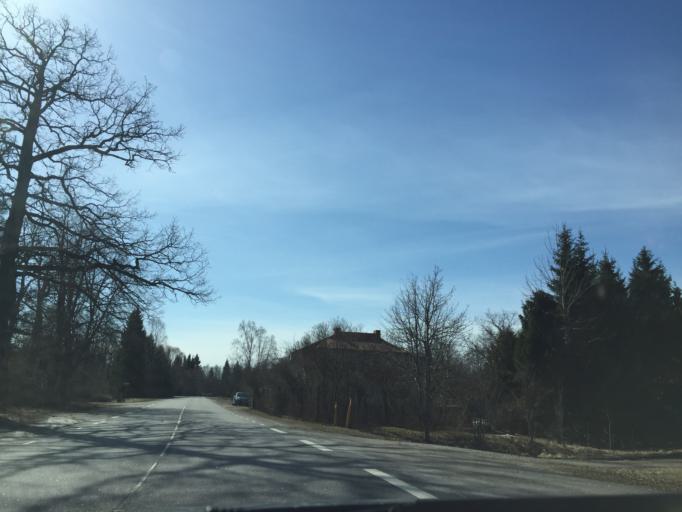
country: EE
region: Laeaene
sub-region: Lihula vald
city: Lihula
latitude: 58.6179
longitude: 23.6915
